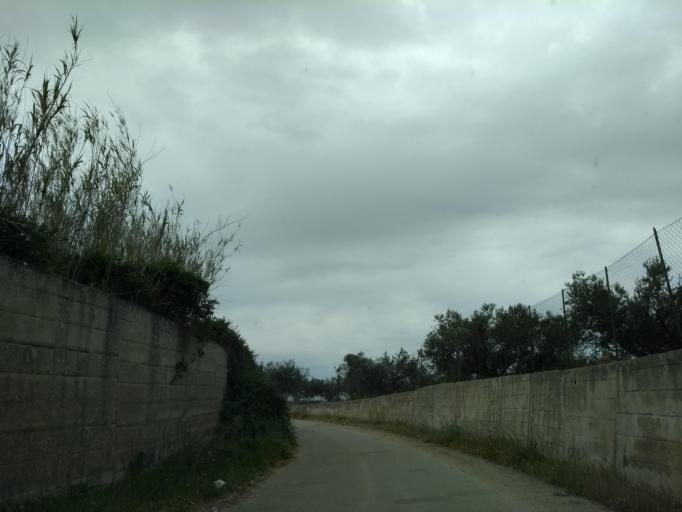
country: IT
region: Sicily
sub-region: Palermo
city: Partinico
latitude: 37.9946
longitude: 13.0796
